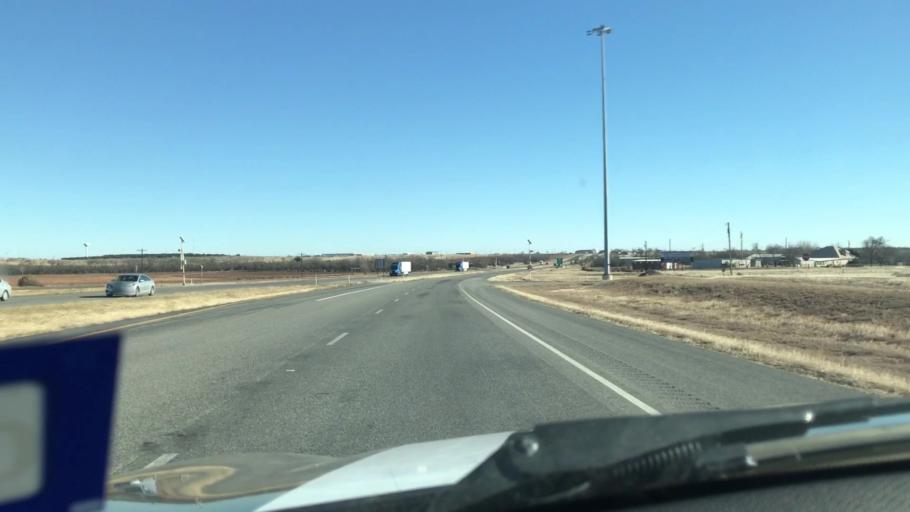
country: US
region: Texas
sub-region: Scurry County
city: Snyder
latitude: 32.7221
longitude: -100.8861
